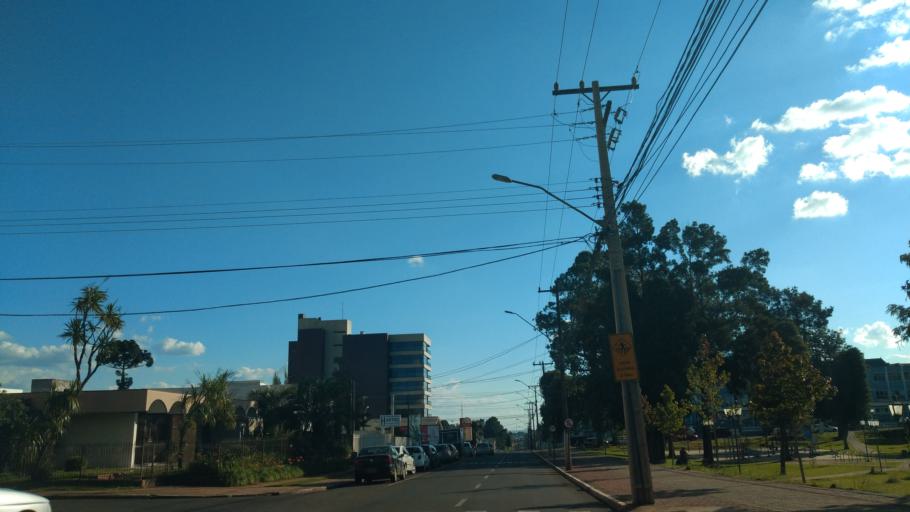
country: BR
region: Parana
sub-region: Guarapuava
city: Guarapuava
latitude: -25.3959
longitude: -51.4617
